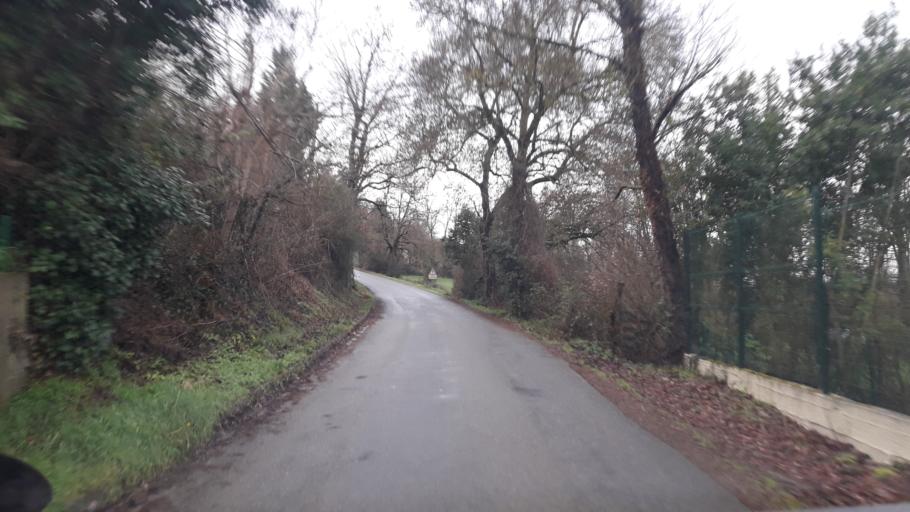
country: FR
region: Midi-Pyrenees
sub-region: Departement de la Haute-Garonne
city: Marquefave
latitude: 43.3158
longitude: 1.2449
